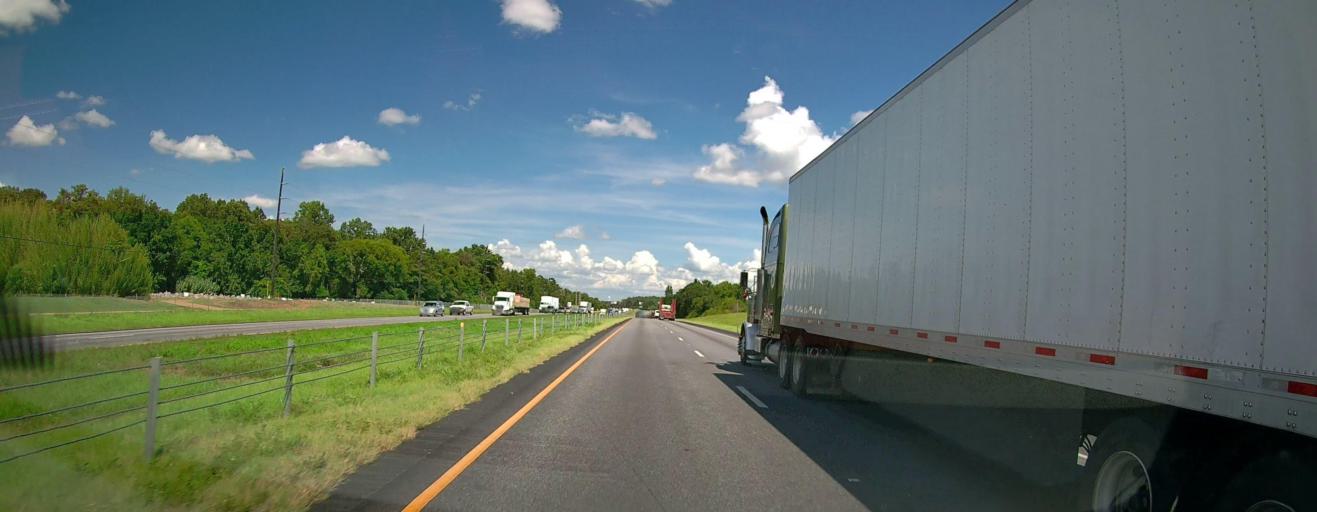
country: US
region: Alabama
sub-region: Montgomery County
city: Pike Road
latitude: 32.3676
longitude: -86.1129
